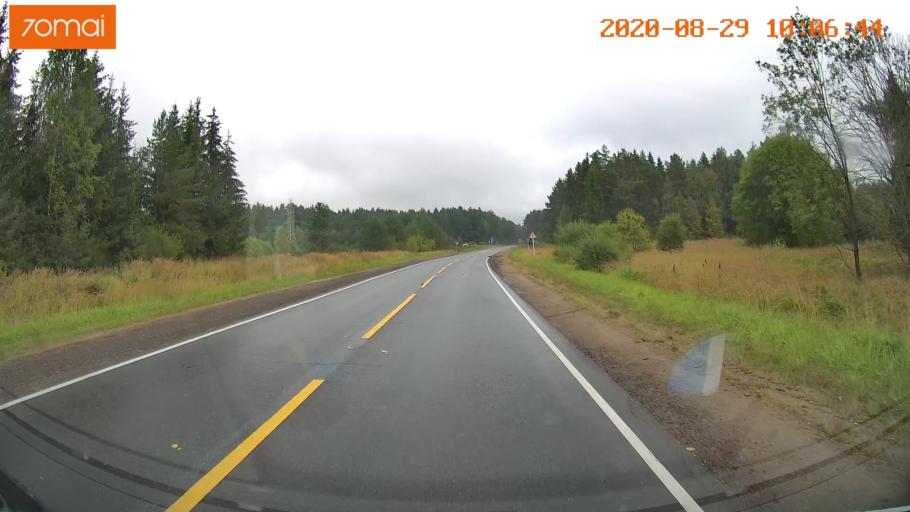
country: RU
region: Ivanovo
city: Kuznechikha
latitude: 57.3868
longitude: 42.5522
